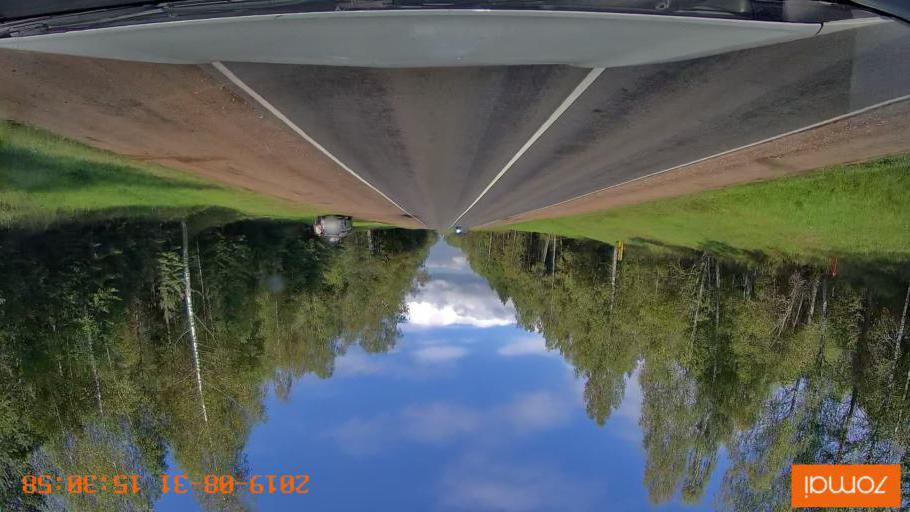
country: RU
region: Kaluga
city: Baryatino
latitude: 54.5793
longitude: 34.6431
